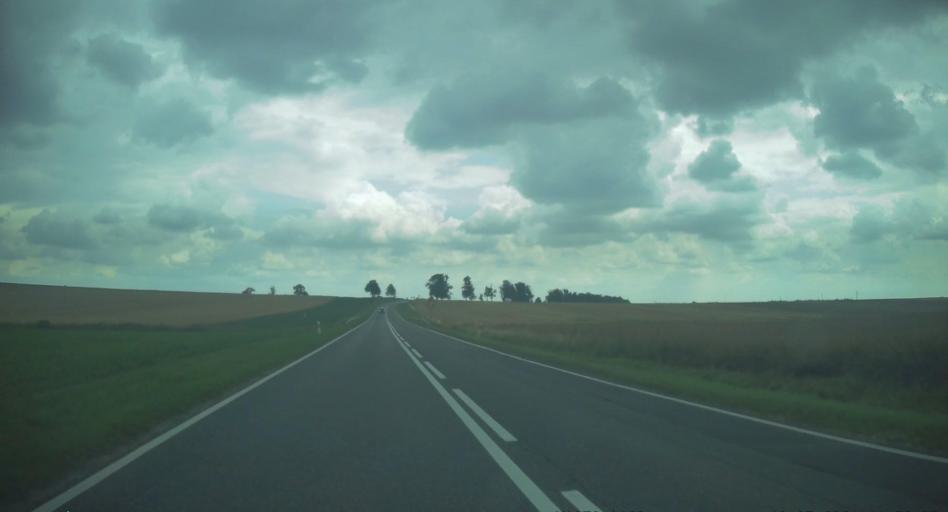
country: PL
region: Opole Voivodeship
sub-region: Powiat prudnicki
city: Moszczanka
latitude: 50.4196
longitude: 17.4754
